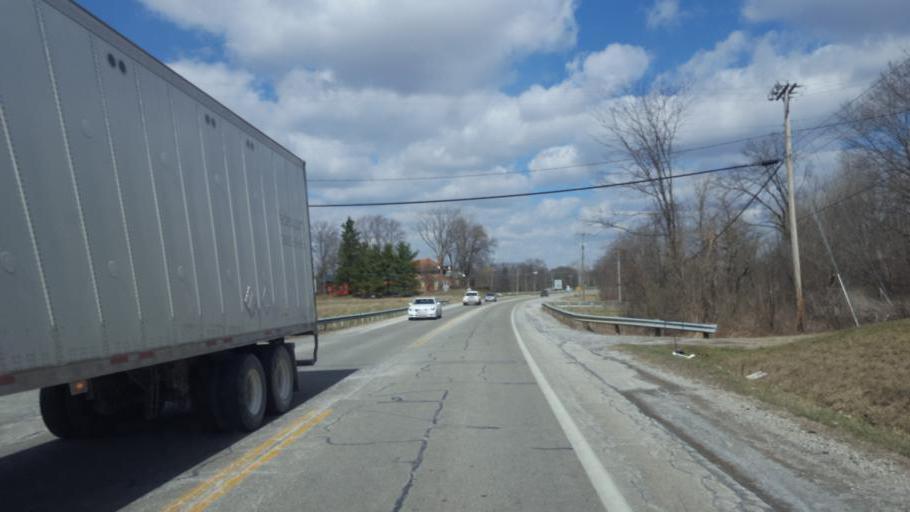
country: US
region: Ohio
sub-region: Knox County
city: Mount Vernon
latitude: 40.3908
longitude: -82.5072
